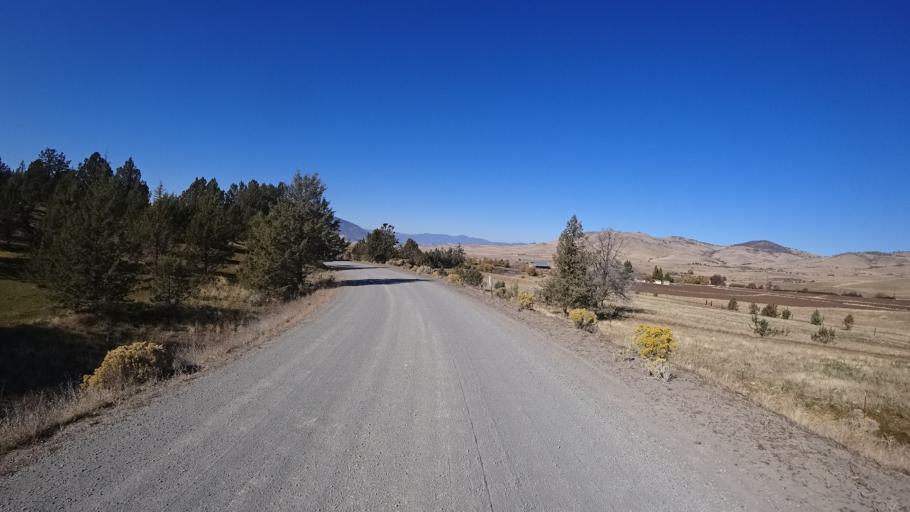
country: US
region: California
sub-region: Siskiyou County
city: Montague
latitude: 41.8076
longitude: -122.3725
